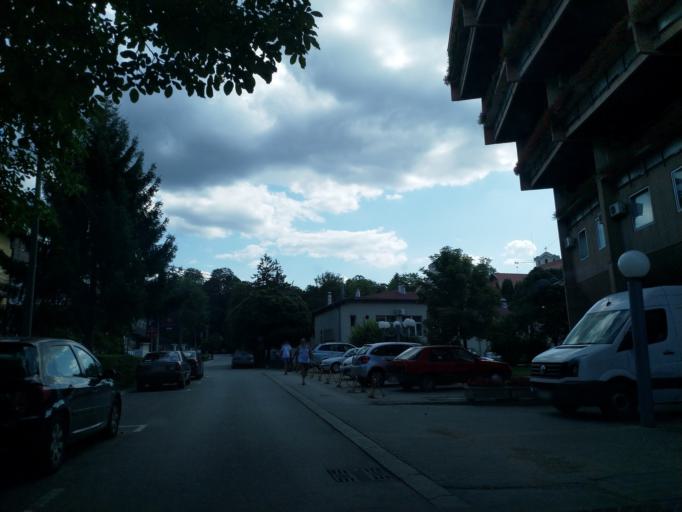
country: RS
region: Central Serbia
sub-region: Raski Okrug
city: Vrnjacka Banja
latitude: 43.6220
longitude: 20.8953
